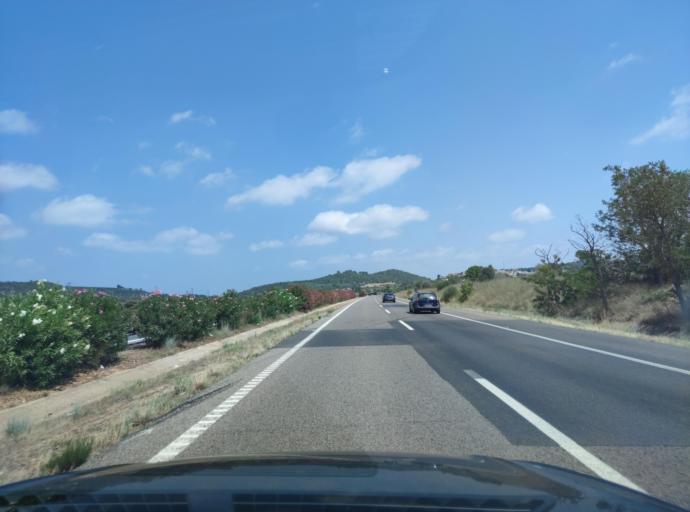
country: ES
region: Catalonia
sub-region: Provincia de Tarragona
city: Santa Barbara
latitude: 40.6610
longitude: 0.5114
